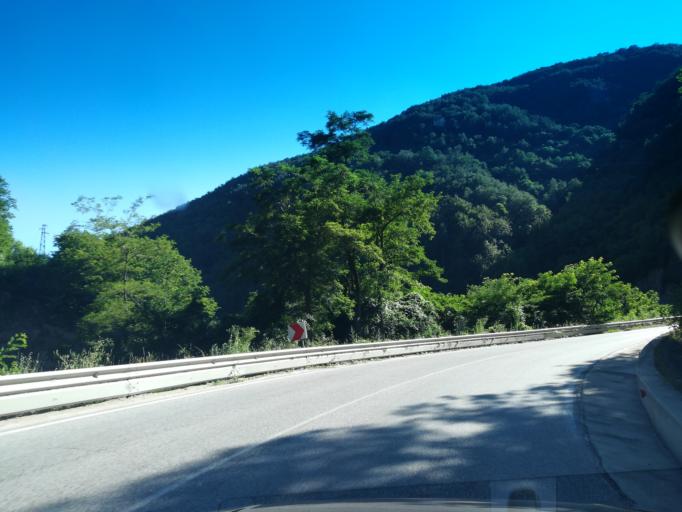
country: BG
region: Smolyan
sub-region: Obshtina Chepelare
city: Chepelare
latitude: 41.7987
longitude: 24.7103
